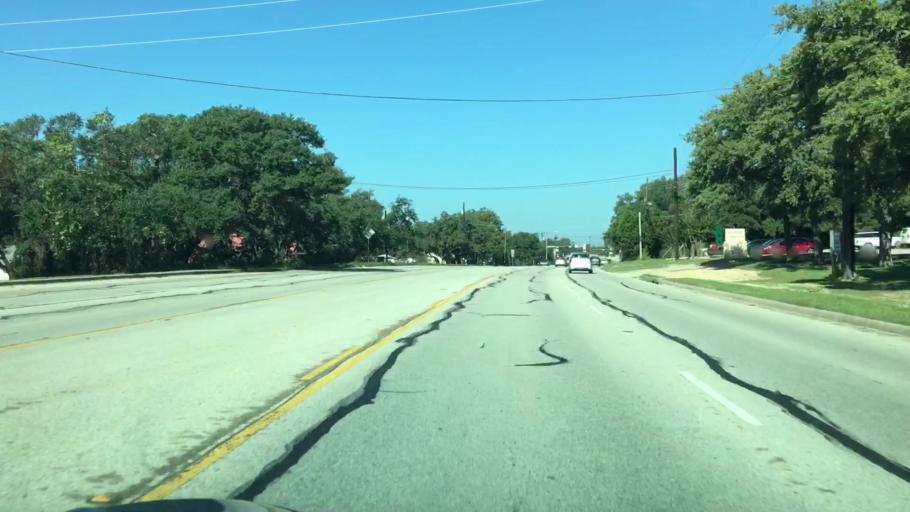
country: US
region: Texas
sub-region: Hays County
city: Dripping Springs
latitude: 30.1930
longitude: -98.0991
